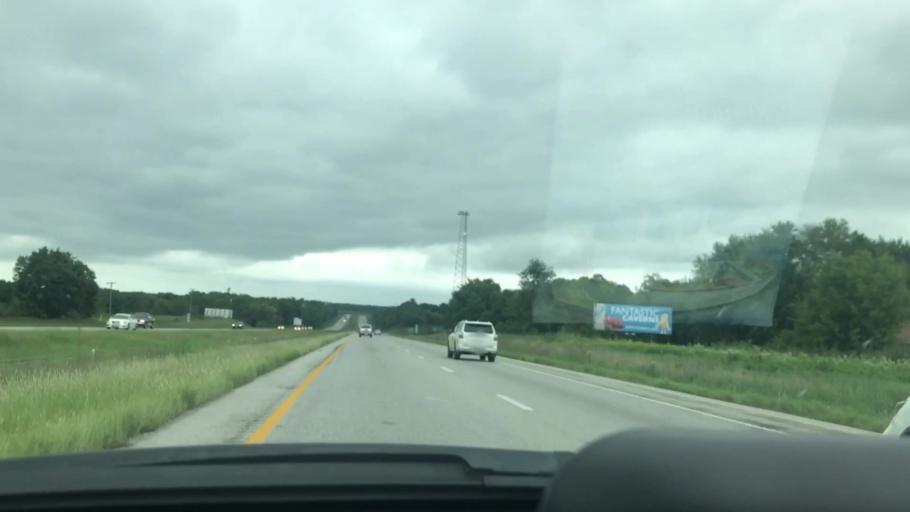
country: US
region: Missouri
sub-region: Jasper County
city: Duenweg
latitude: 37.0751
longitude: -94.3864
